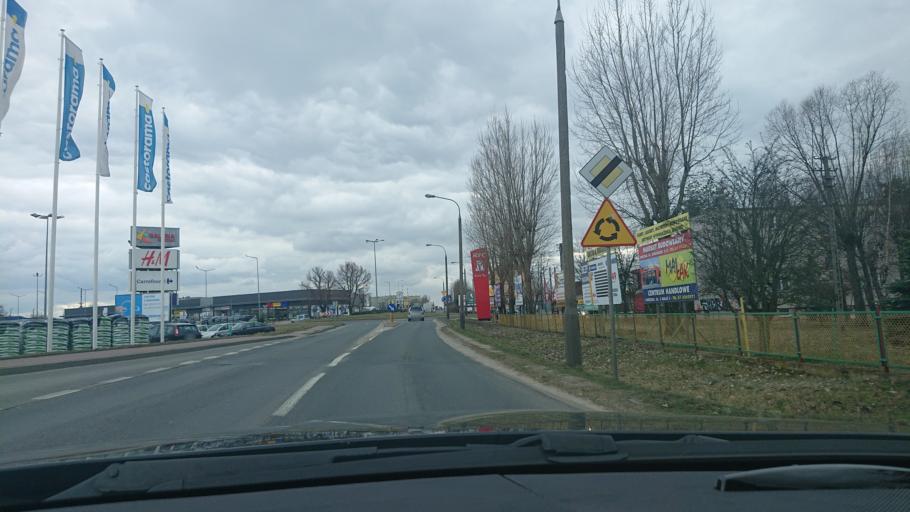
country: PL
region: Greater Poland Voivodeship
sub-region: Powiat gnieznienski
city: Gniezno
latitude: 52.5626
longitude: 17.6102
